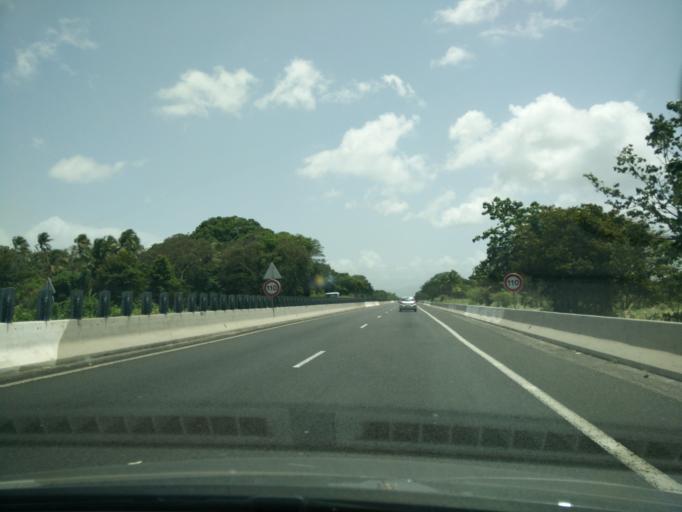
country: GP
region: Guadeloupe
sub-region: Guadeloupe
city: Baie-Mahault
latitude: 16.2695
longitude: -61.5538
